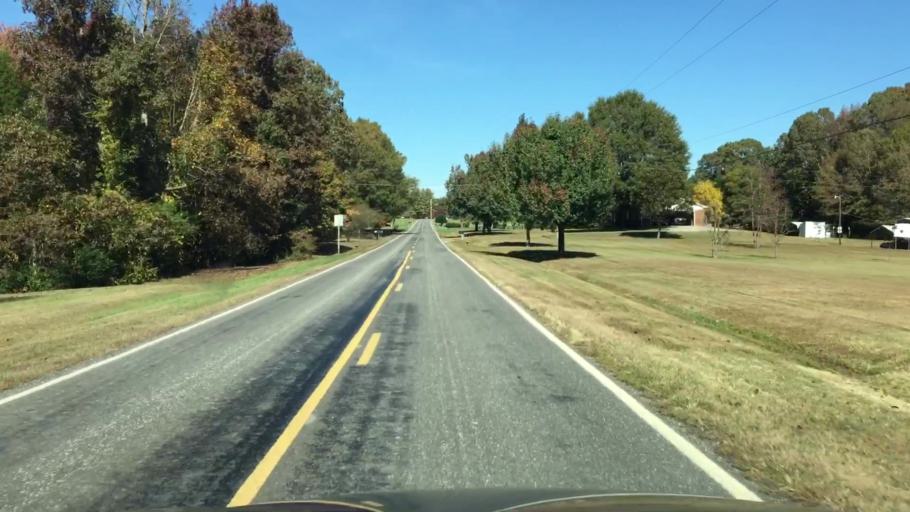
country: US
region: North Carolina
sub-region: Iredell County
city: Mooresville
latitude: 35.5811
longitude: -80.7616
